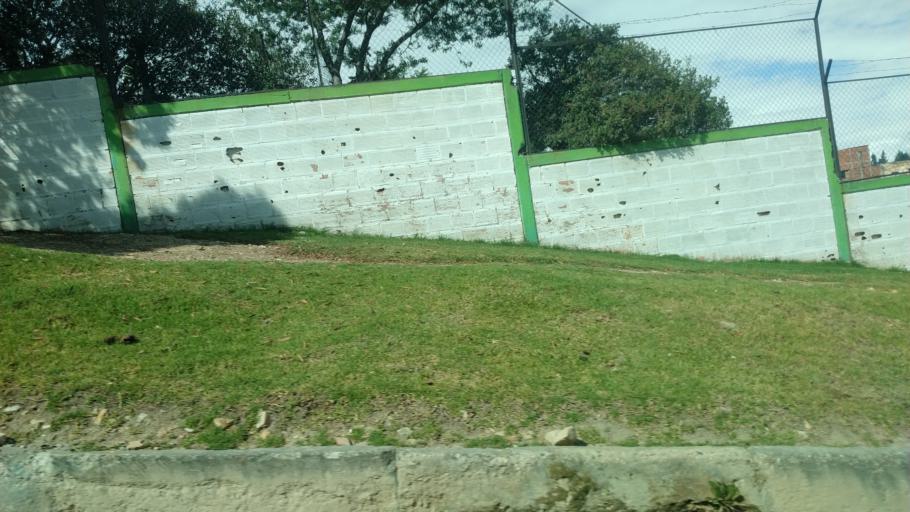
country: CO
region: Cundinamarca
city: Soacha
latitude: 4.5686
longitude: -74.1868
